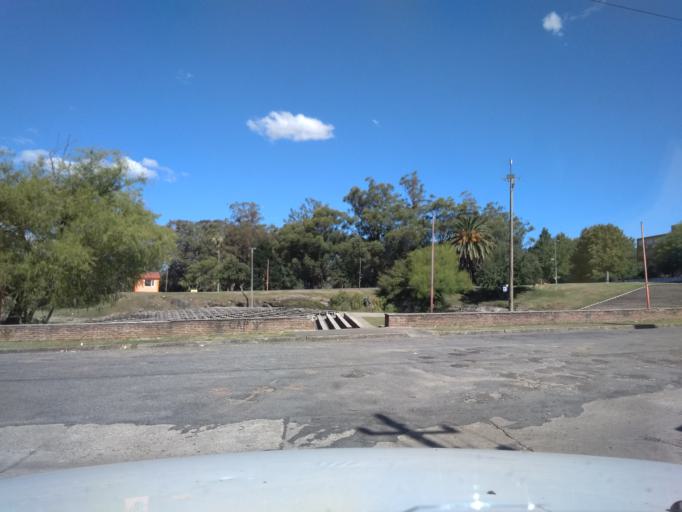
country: UY
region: Florida
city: Florida
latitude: -34.0975
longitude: -56.2072
